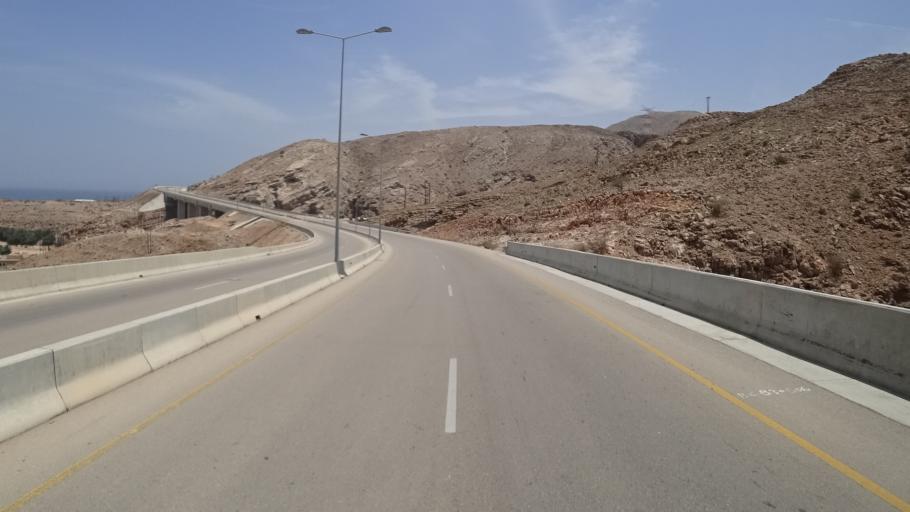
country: OM
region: Ash Sharqiyah
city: Sur
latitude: 22.6972
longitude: 59.3652
